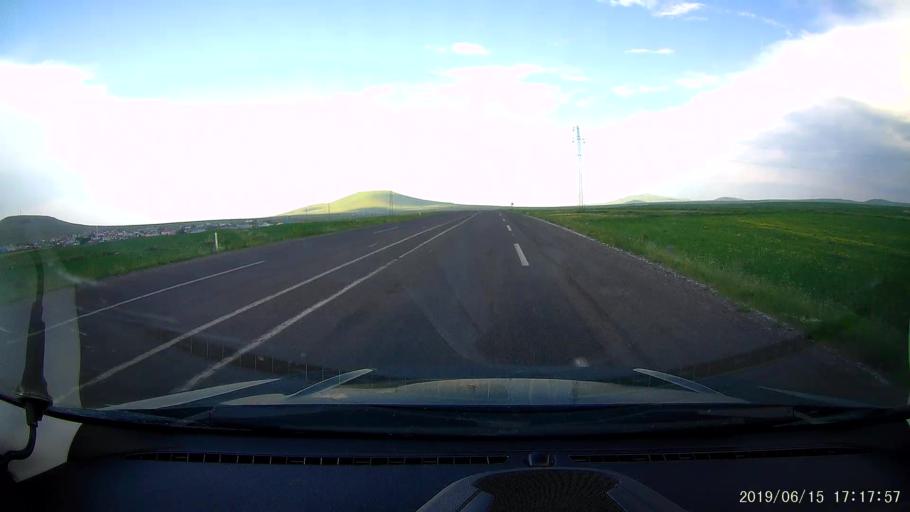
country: TR
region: Kars
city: Kars
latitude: 40.6142
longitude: 43.2484
